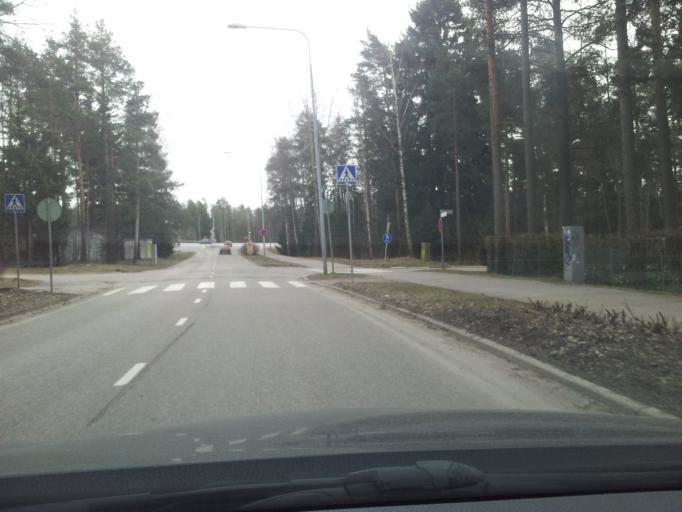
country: FI
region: Uusimaa
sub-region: Helsinki
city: Otaniemi
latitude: 60.2046
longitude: 24.8123
